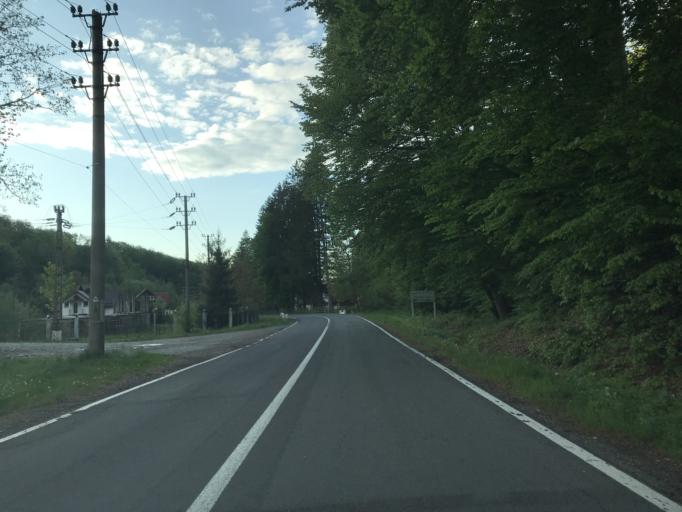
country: RO
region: Sibiu
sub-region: Comuna Cartisoara
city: Cartisoara
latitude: 45.6817
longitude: 24.5769
